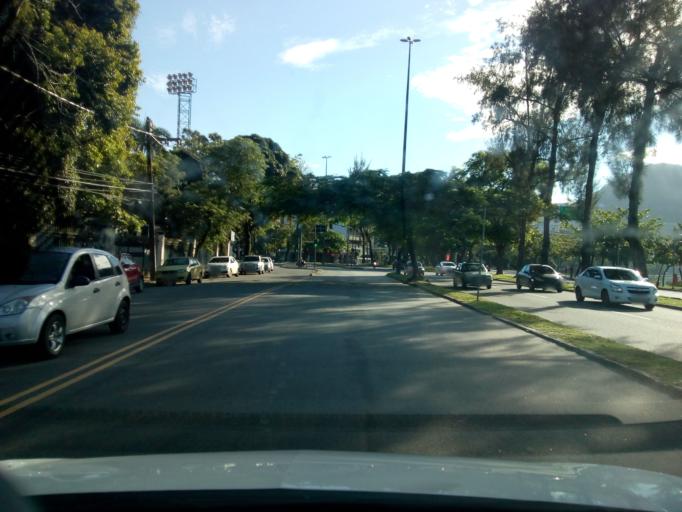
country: BR
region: Rio de Janeiro
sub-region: Rio De Janeiro
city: Rio de Janeiro
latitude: -22.9635
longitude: -43.2134
